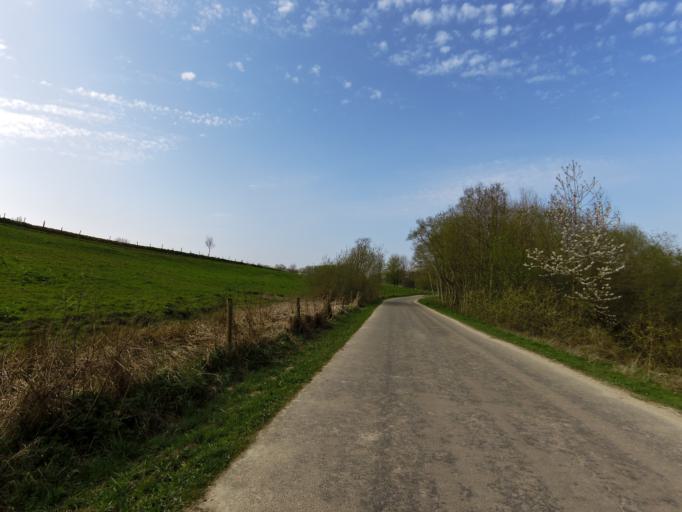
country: NL
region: Limburg
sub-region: Gemeente Kerkrade
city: Kerkrade
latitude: 50.8765
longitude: 6.0508
